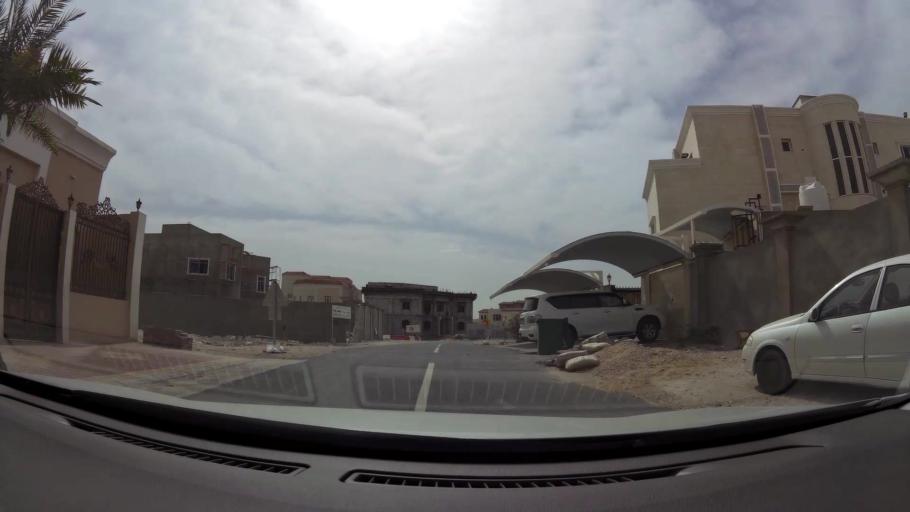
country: QA
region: Baladiyat ad Dawhah
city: Doha
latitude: 25.2189
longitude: 51.4862
